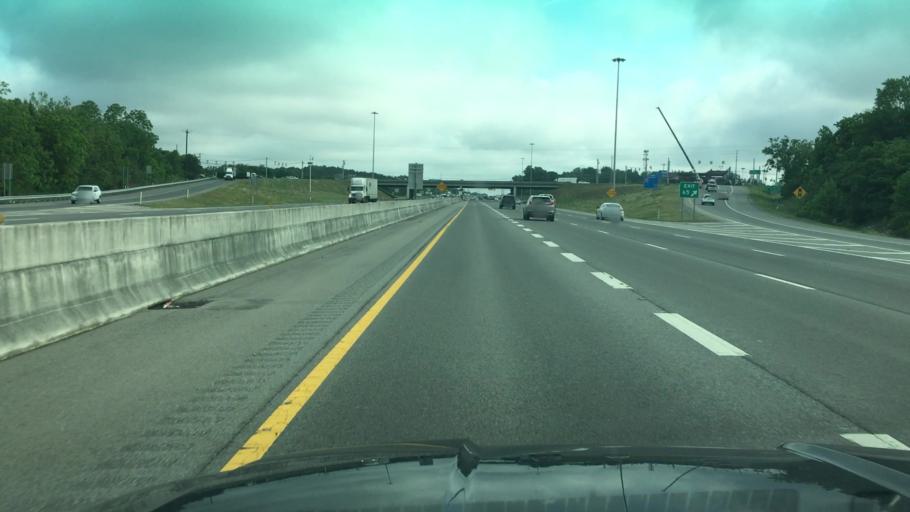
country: US
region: Tennessee
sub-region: Williamson County
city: Franklin
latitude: 35.9111
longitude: -86.8246
